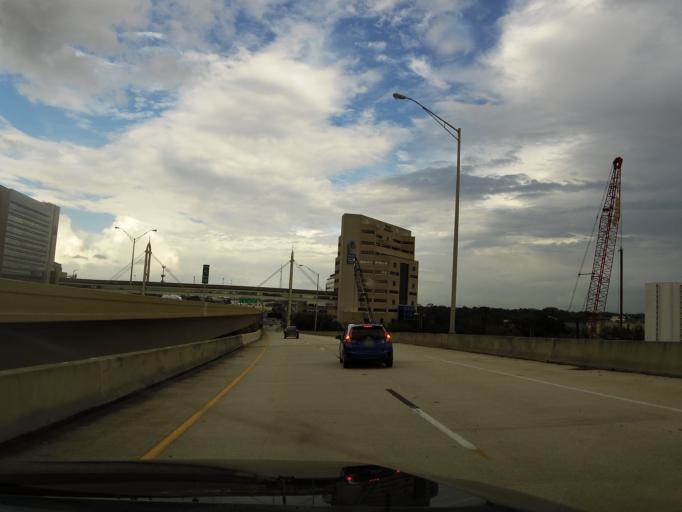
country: US
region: Florida
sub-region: Duval County
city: Jacksonville
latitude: 30.3138
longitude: -81.6660
